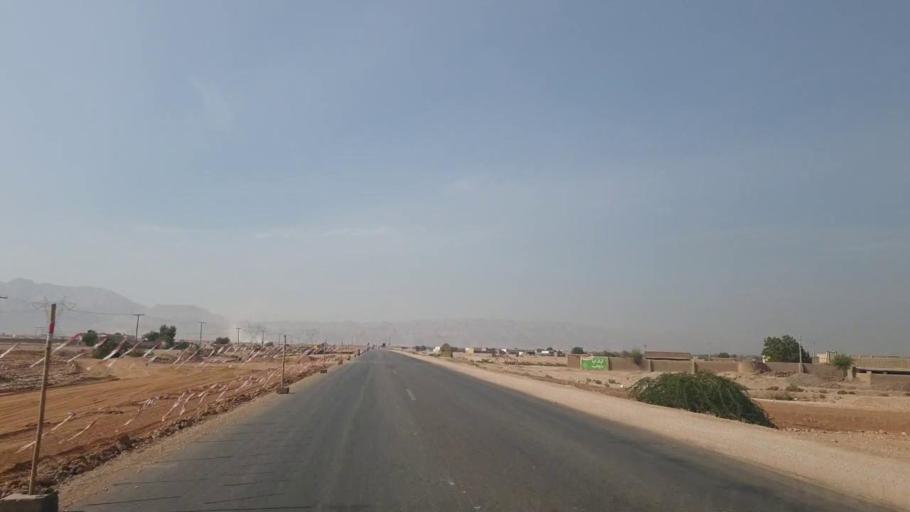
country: PK
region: Sindh
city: Sehwan
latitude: 26.2013
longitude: 67.9373
